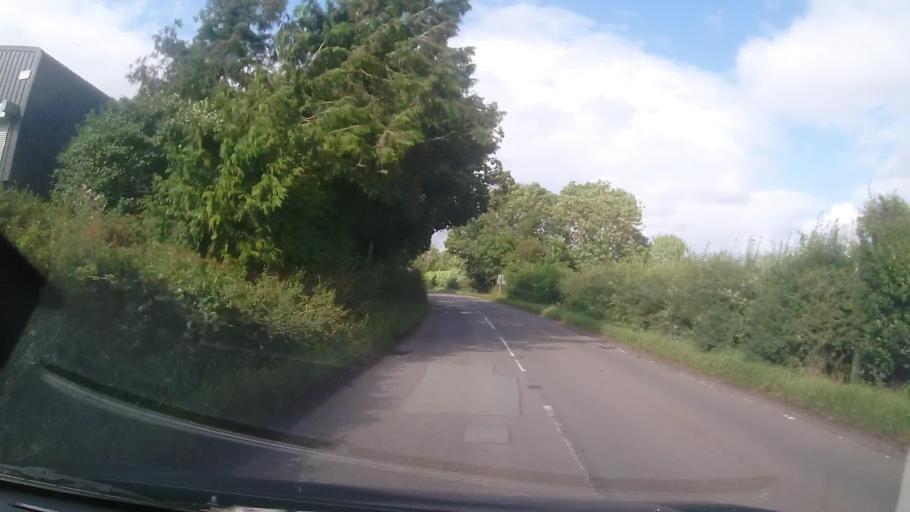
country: GB
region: England
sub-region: Shropshire
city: Bishop's Castle
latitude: 52.4916
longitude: -2.9909
